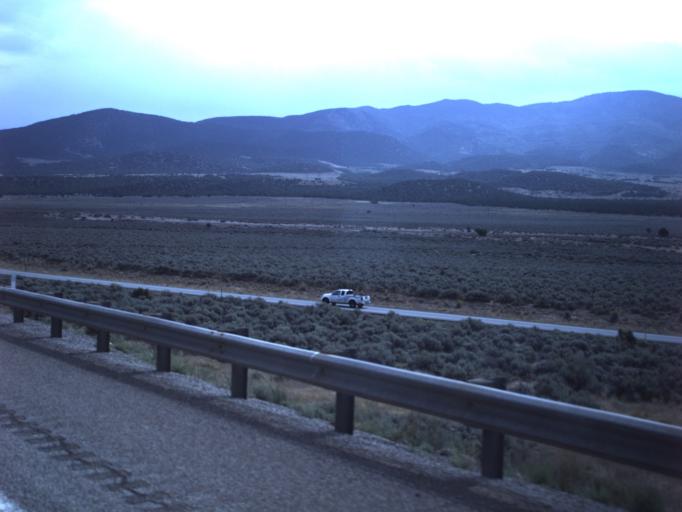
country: US
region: Utah
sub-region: Beaver County
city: Beaver
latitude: 38.5775
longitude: -112.6028
